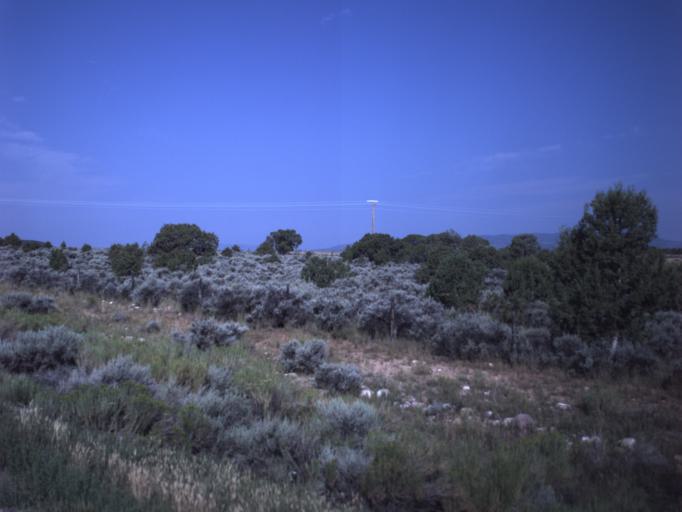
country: US
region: Utah
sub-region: Duchesne County
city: Duchesne
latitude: 40.3488
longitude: -110.4053
